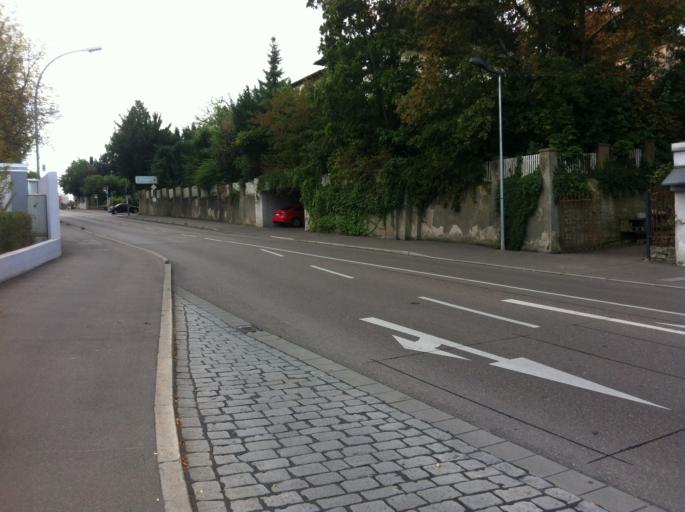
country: DE
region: Baden-Wuerttemberg
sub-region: Regierungsbezirk Stuttgart
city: Kornwestheim
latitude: 48.8638
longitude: 9.1858
